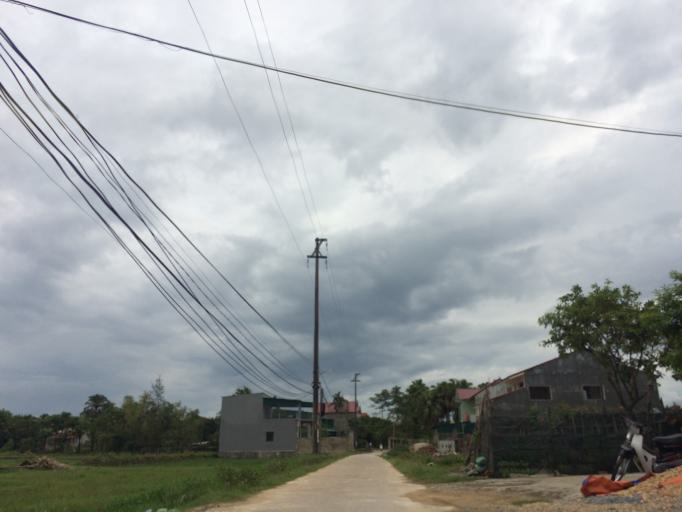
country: VN
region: Ha Tinh
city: Ha Tinh
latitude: 18.3350
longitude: 105.8763
